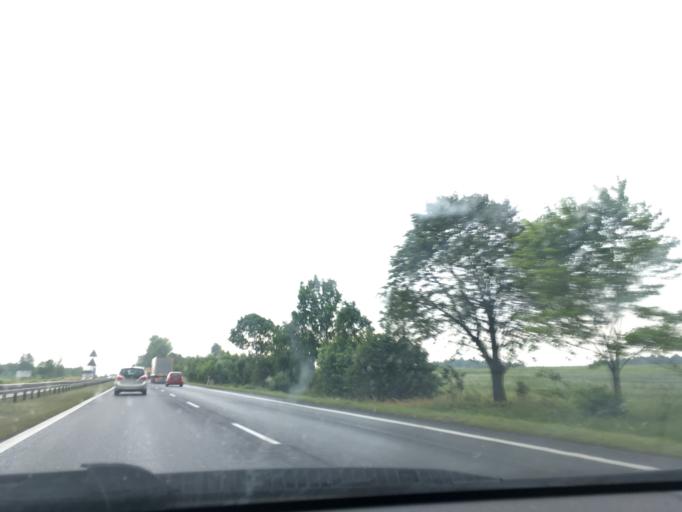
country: PL
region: Silesian Voivodeship
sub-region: Powiat bedzinski
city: Siewierz
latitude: 50.4423
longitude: 19.2206
